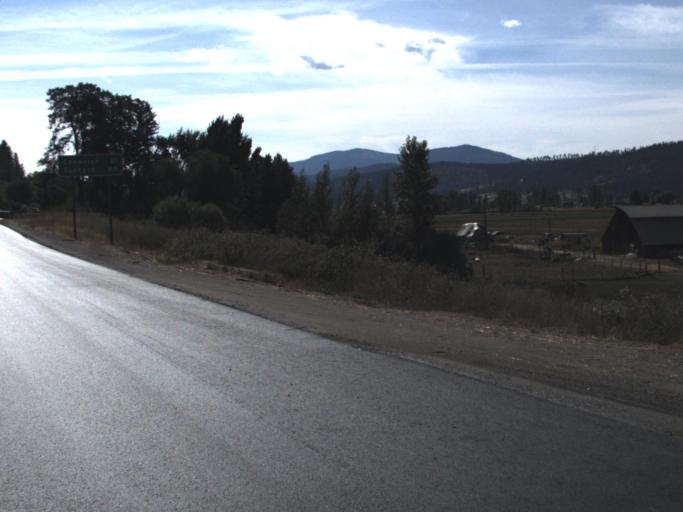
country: US
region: Washington
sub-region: Stevens County
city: Colville
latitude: 48.5286
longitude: -117.9030
